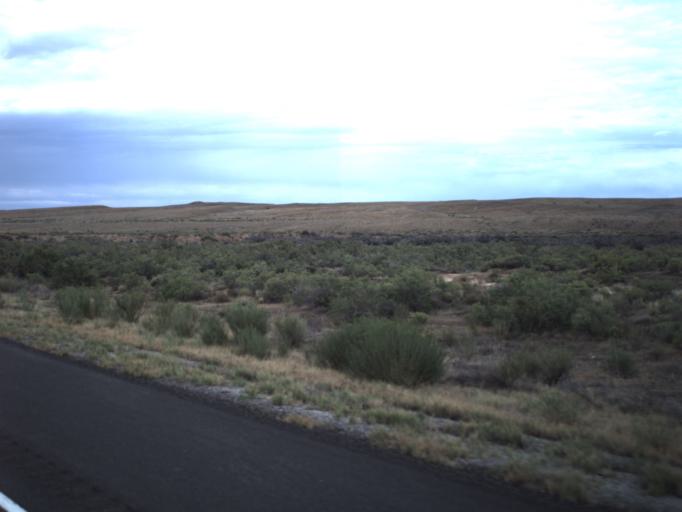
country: US
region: Colorado
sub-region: Mesa County
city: Loma
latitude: 39.0798
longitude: -109.2272
